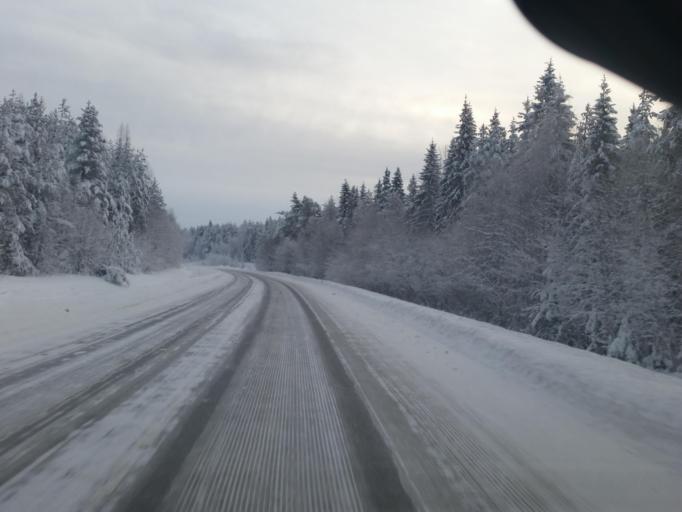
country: SE
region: Norrbotten
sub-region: Pitea Kommun
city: Norrfjarden
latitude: 65.6368
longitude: 21.3499
